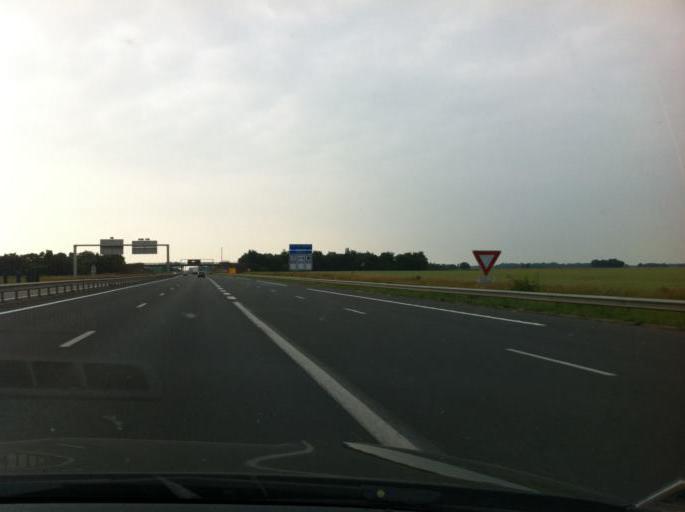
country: FR
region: Ile-de-France
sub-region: Departement de Seine-et-Marne
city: Vert-Saint-Denis
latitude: 48.5973
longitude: 2.6351
